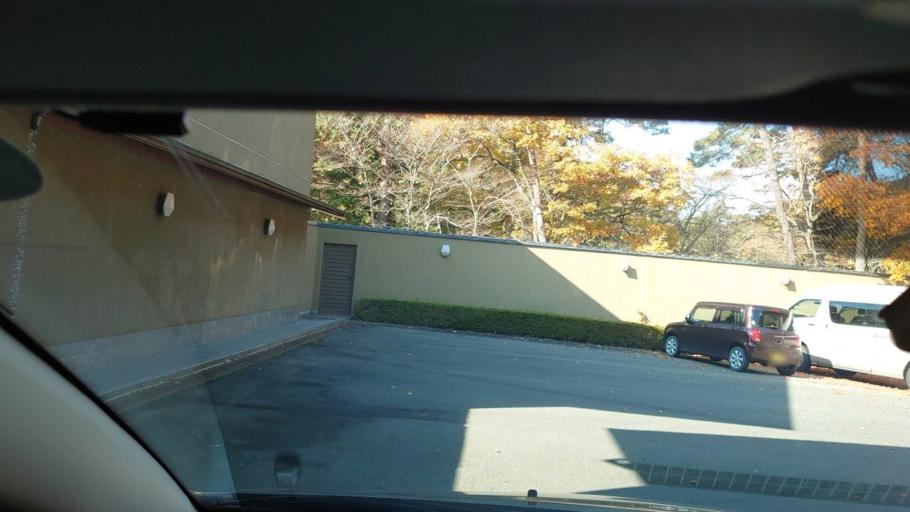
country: JP
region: Iwate
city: Hanamaki
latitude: 39.4554
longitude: 141.0670
